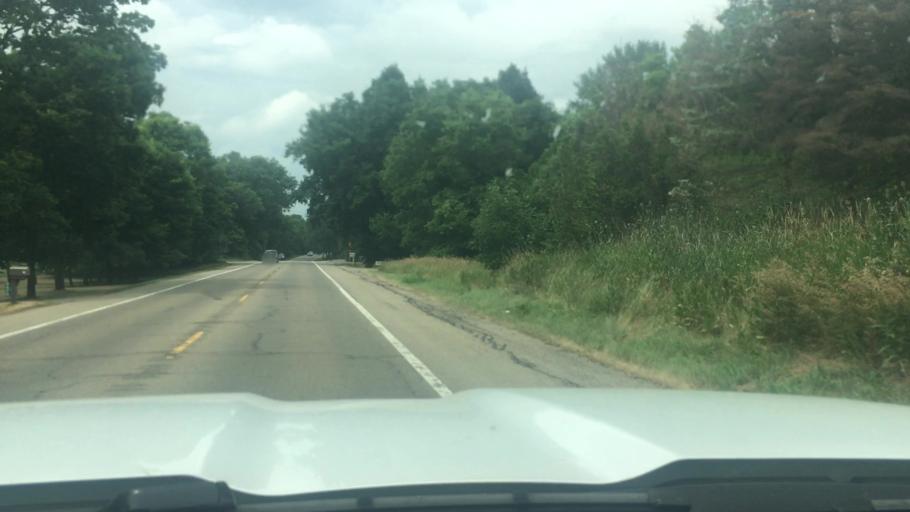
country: US
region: Michigan
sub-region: Kent County
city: Forest Hills
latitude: 42.9307
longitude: -85.4339
